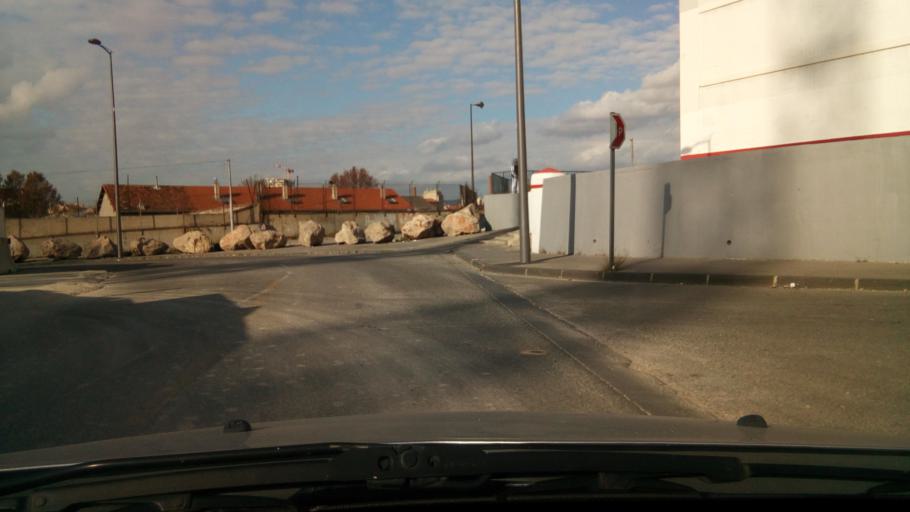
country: FR
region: Provence-Alpes-Cote d'Azur
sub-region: Departement des Bouches-du-Rhone
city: Marseille 03
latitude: 43.3174
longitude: 5.3726
